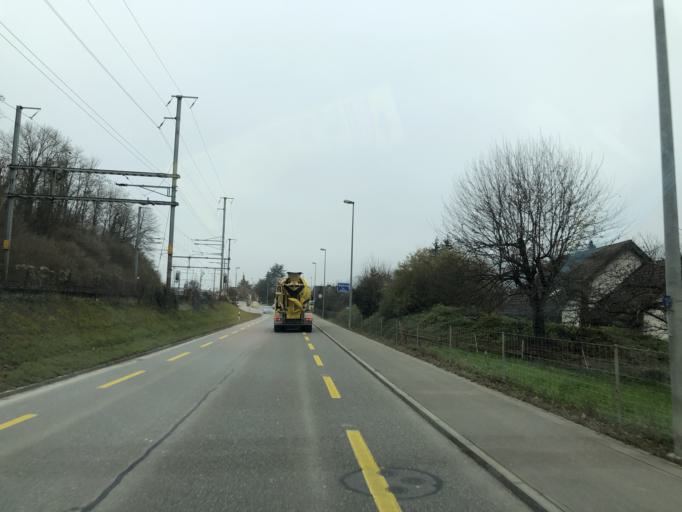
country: CH
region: Aargau
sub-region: Bezirk Baden
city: Turgi
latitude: 47.4934
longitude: 8.2451
